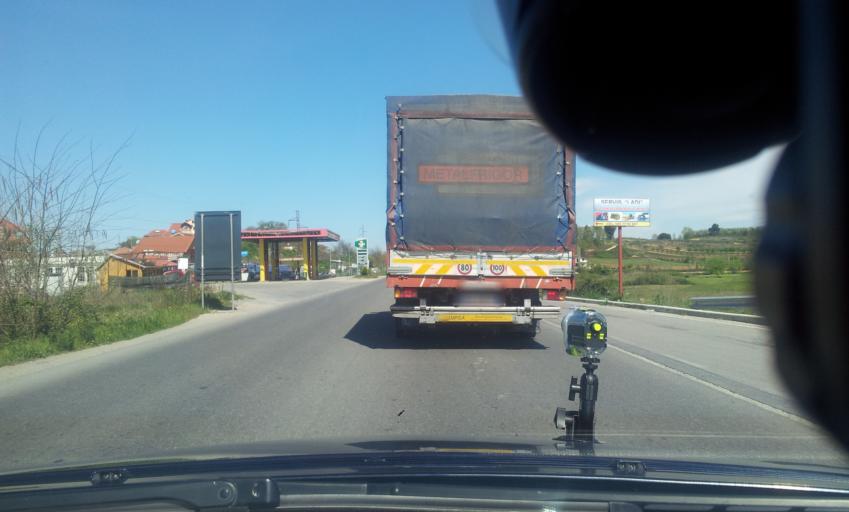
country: AL
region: Durres
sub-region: Rrethi i Krujes
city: Hasan
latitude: 41.4924
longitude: 19.7035
